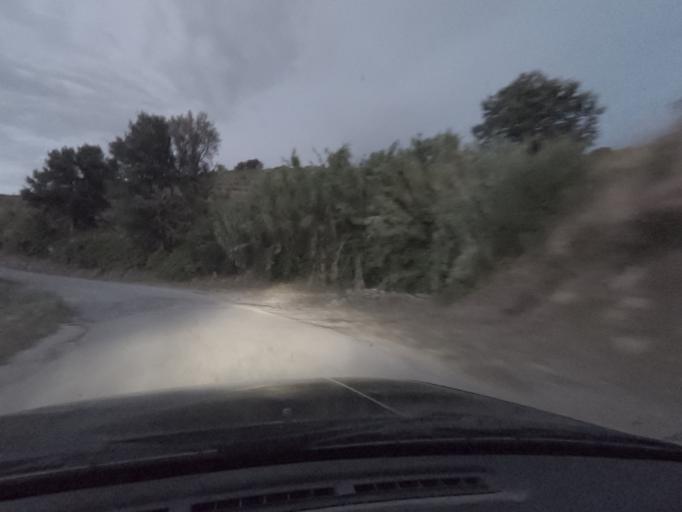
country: PT
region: Vila Real
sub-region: Peso da Regua
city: Godim
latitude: 41.1672
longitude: -7.8324
